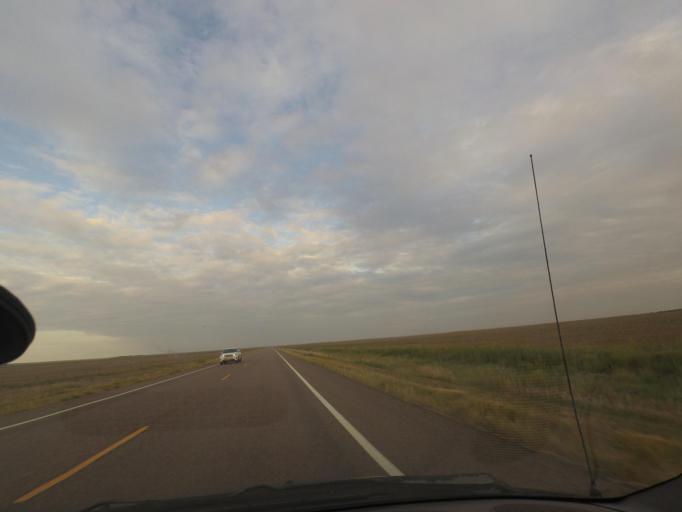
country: US
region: Kansas
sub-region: Cheyenne County
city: Saint Francis
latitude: 39.7459
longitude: -102.1258
